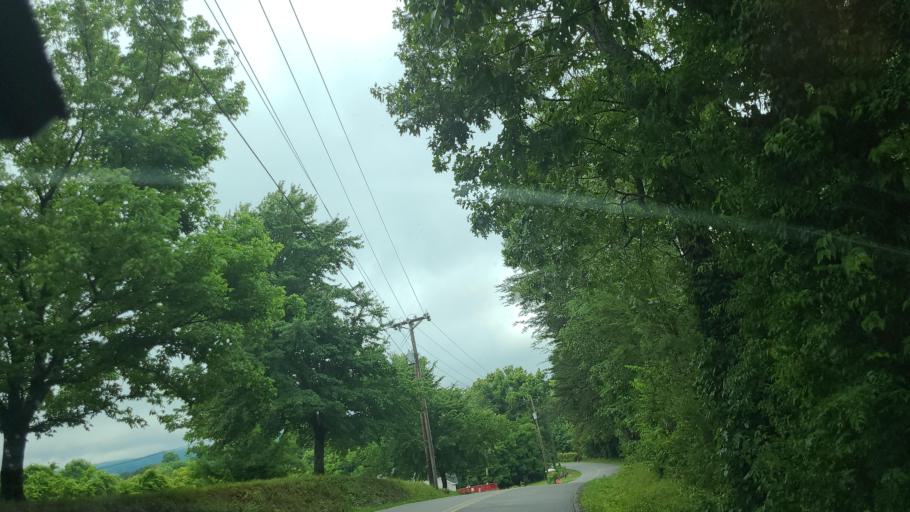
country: US
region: Tennessee
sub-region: Rhea County
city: Dayton
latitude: 35.5048
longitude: -84.9858
